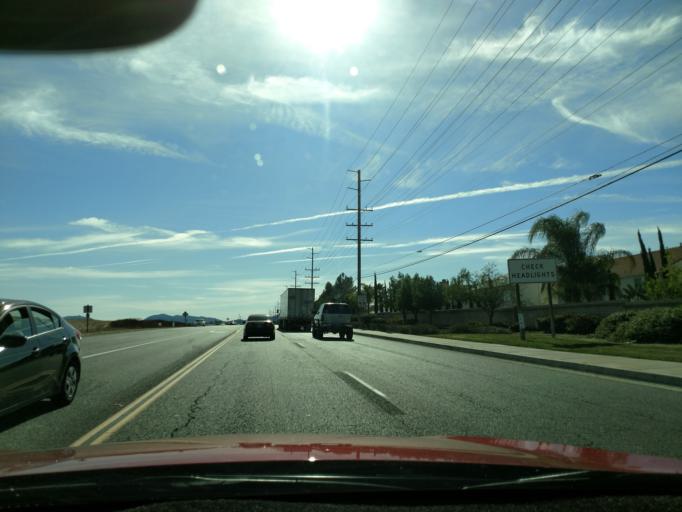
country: US
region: California
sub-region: Riverside County
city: Murrieta Hot Springs
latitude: 33.5685
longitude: -117.1367
